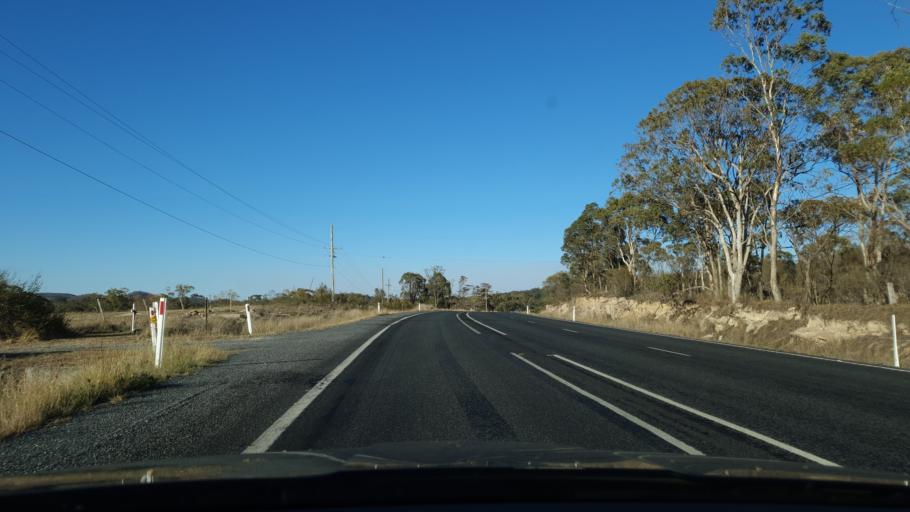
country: AU
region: Queensland
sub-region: Southern Downs
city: Stanthorpe
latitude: -28.6868
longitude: 151.9121
